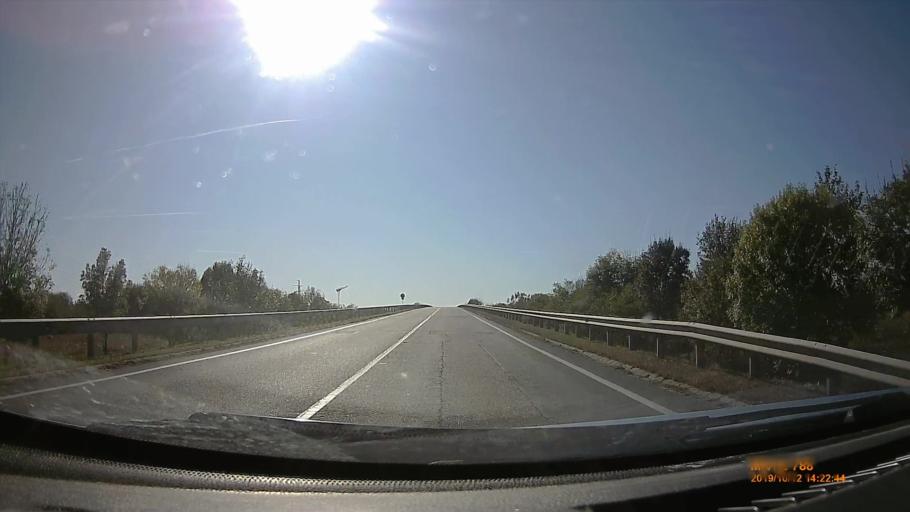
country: HU
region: Hajdu-Bihar
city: Biharkeresztes
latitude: 47.1410
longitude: 21.7105
